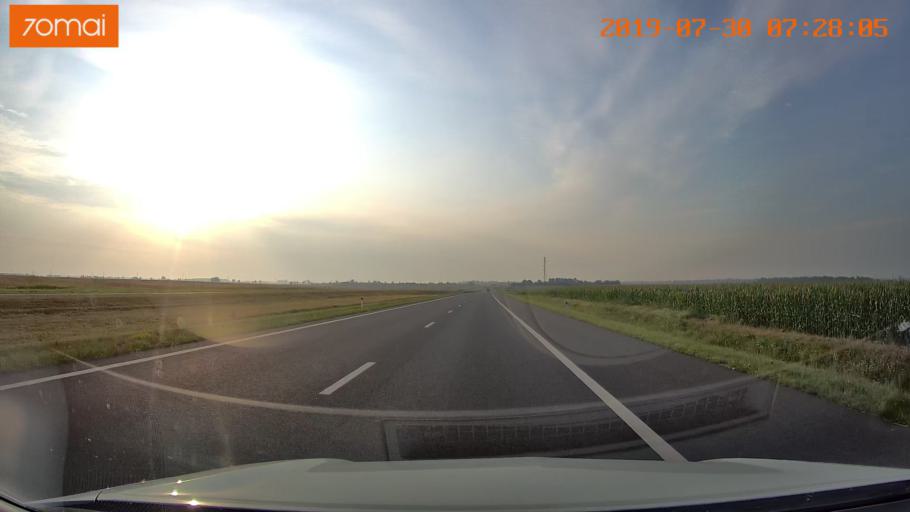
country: RU
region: Kaliningrad
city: Gvardeysk
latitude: 54.6790
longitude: 20.9041
